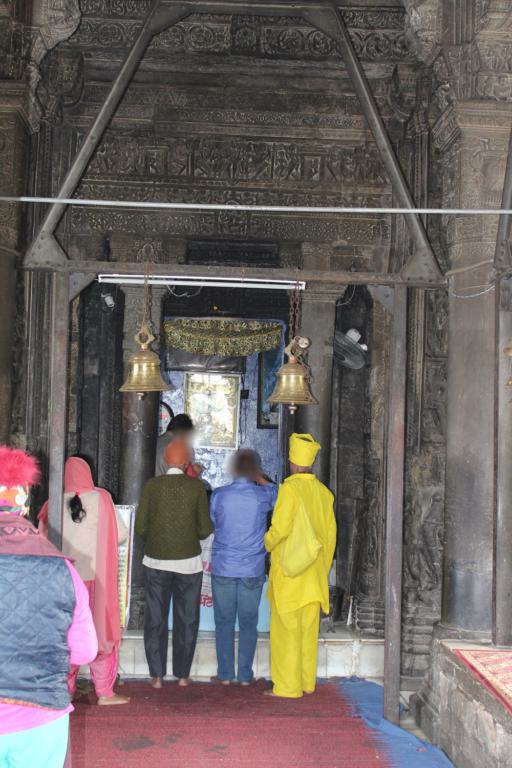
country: IN
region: Himachal Pradesh
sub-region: Kangra
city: Palampur
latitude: 32.0509
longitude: 76.6458
